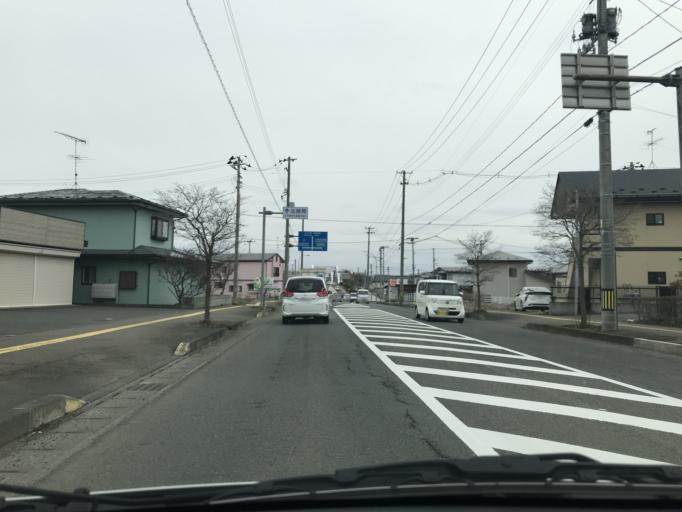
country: JP
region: Iwate
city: Hanamaki
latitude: 39.3833
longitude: 141.1102
